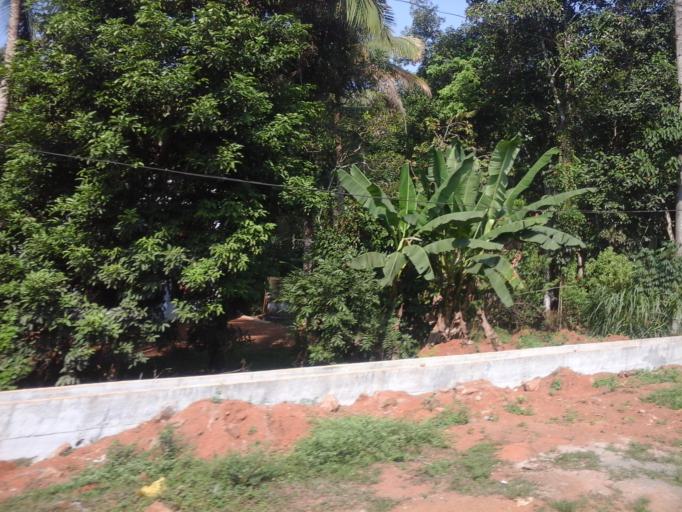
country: IN
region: Kerala
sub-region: Kottayam
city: Lalam
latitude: 9.6965
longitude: 76.6856
